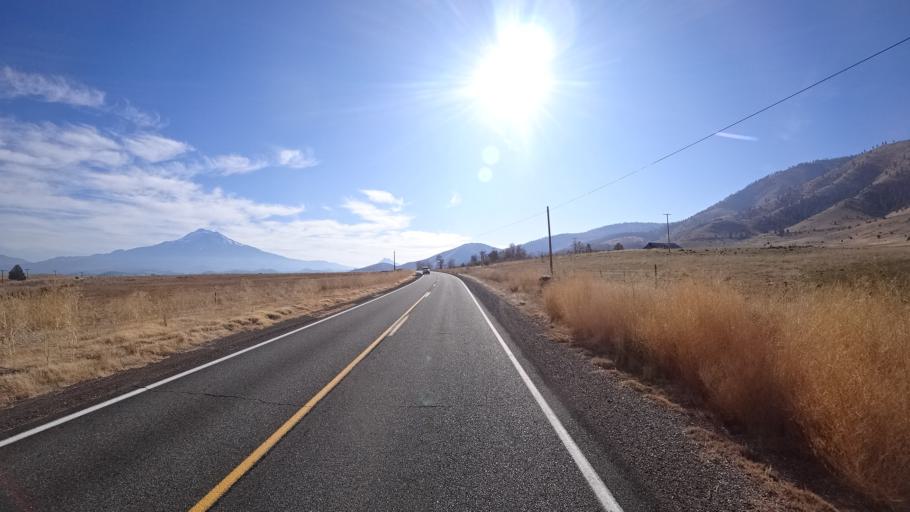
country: US
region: California
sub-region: Siskiyou County
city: Weed
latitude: 41.4929
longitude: -122.5090
